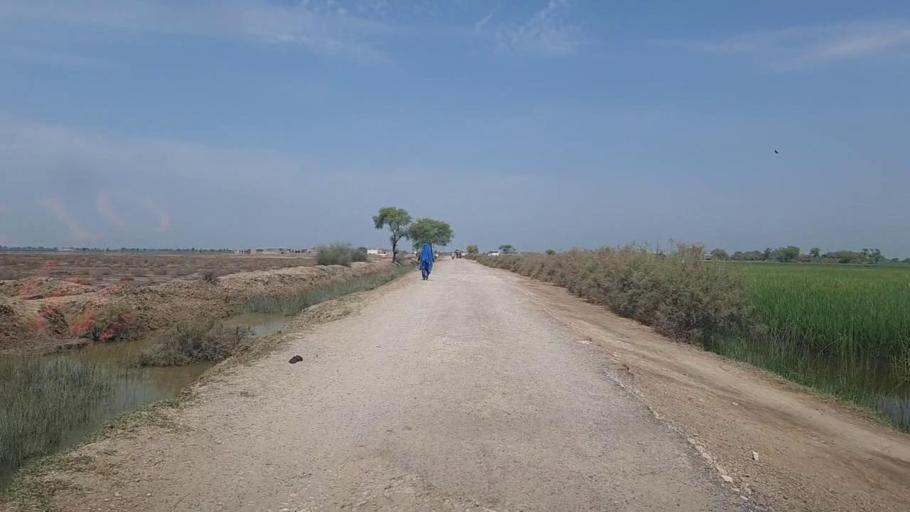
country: PK
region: Sindh
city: Thul
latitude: 28.2885
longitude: 68.6842
